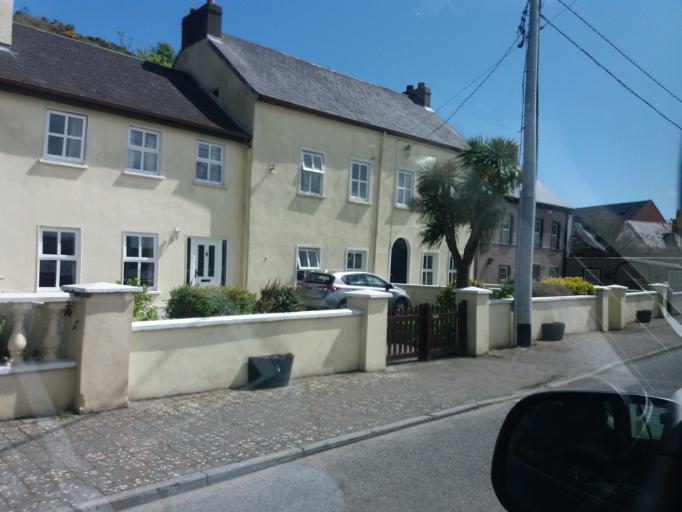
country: IE
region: Munster
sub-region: Waterford
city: Dunmore East
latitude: 52.2454
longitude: -6.9681
